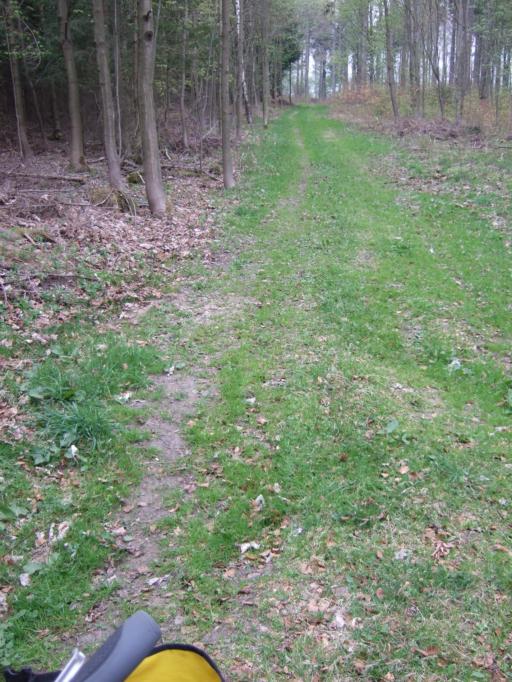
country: DE
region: Saxony
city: Rechenberg-Bienenmuhle
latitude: 50.7443
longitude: 13.5439
